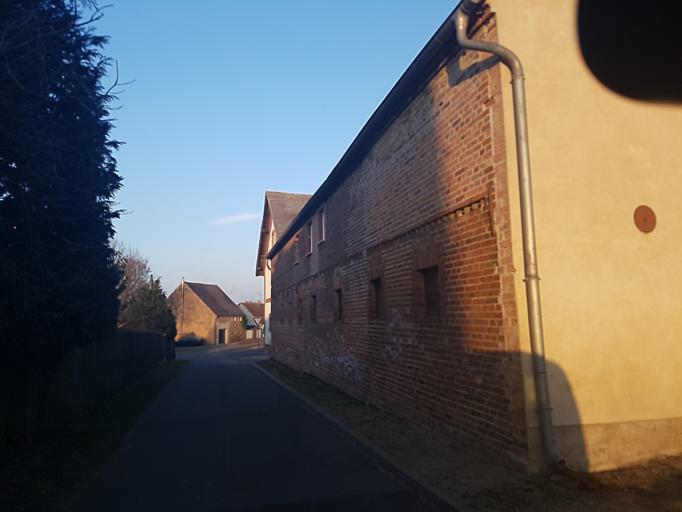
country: DE
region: Brandenburg
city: Juterbog
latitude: 51.9173
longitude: 13.0921
